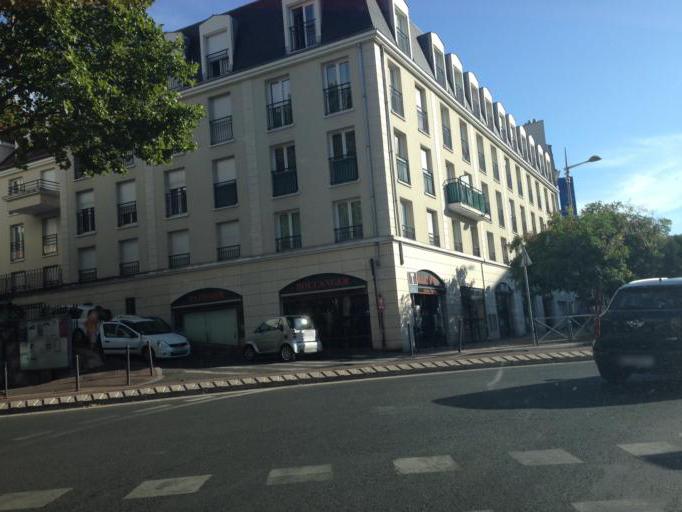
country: FR
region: Ile-de-France
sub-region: Departement des Hauts-de-Seine
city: Meudon
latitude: 48.8180
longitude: 2.2494
